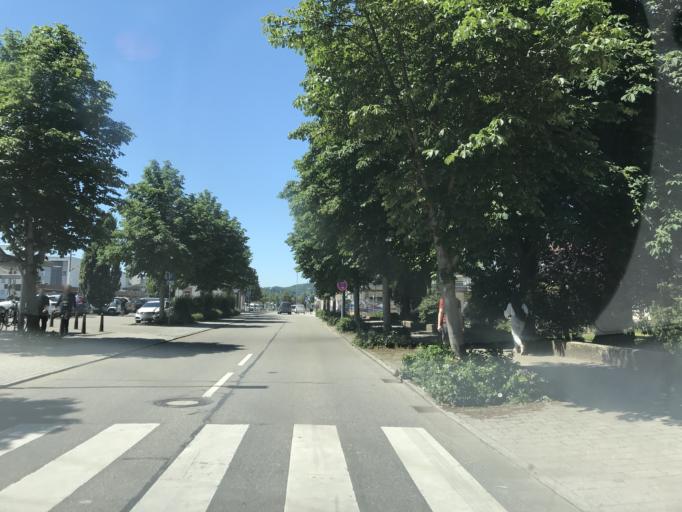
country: DE
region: Baden-Wuerttemberg
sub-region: Freiburg Region
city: Schopfheim
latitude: 47.6487
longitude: 7.8234
